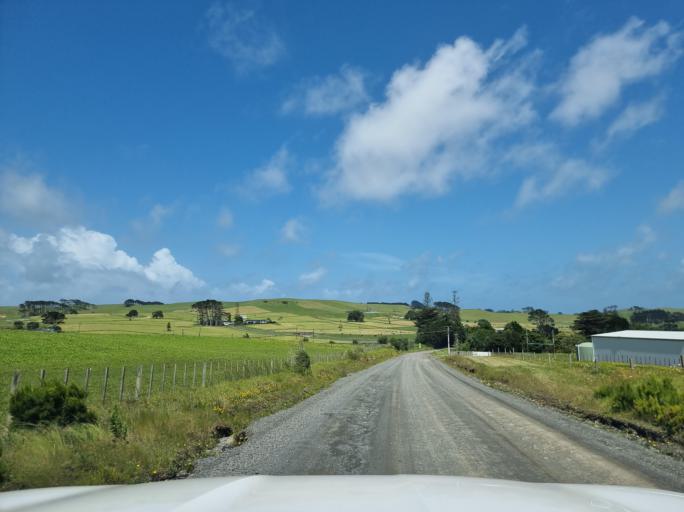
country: NZ
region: Northland
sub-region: Kaipara District
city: Dargaville
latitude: -35.9449
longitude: 173.7863
